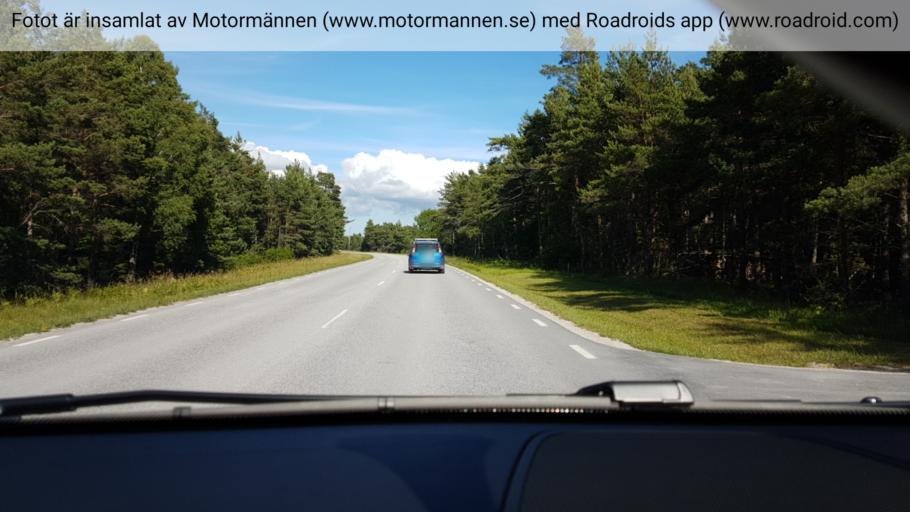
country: SE
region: Gotland
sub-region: Gotland
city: Slite
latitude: 57.7450
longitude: 18.6855
